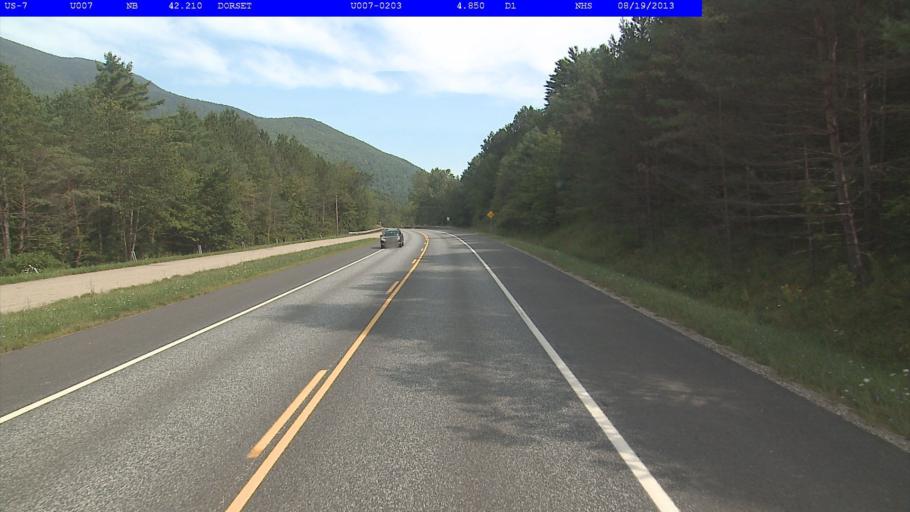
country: US
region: Vermont
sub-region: Bennington County
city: Manchester Center
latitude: 43.2786
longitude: -73.0032
